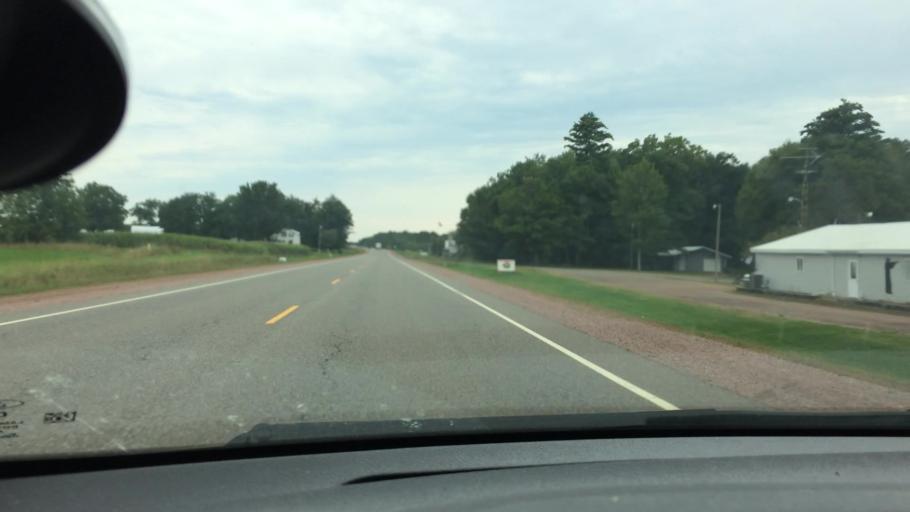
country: US
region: Wisconsin
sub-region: Clark County
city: Neillsville
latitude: 44.5639
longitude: -90.6941
